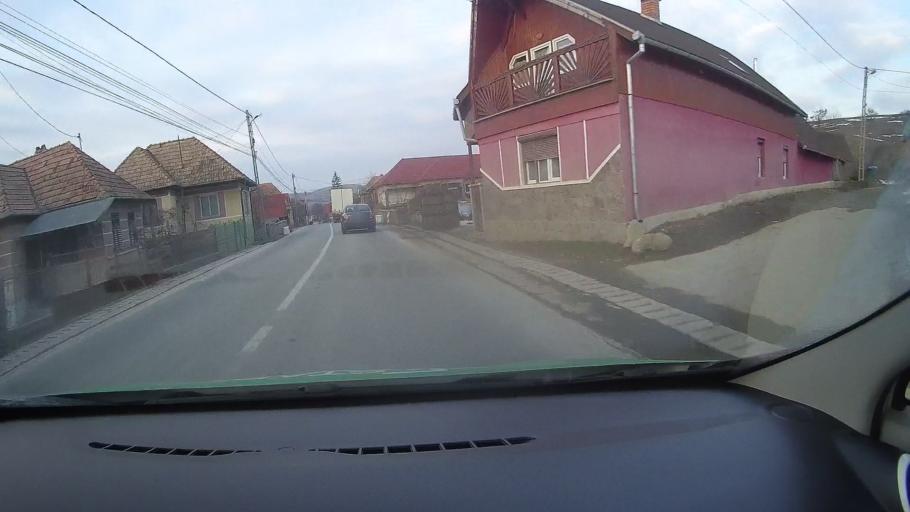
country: RO
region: Harghita
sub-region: Comuna Simonesti
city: Simonesti
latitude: 46.3324
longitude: 25.1063
